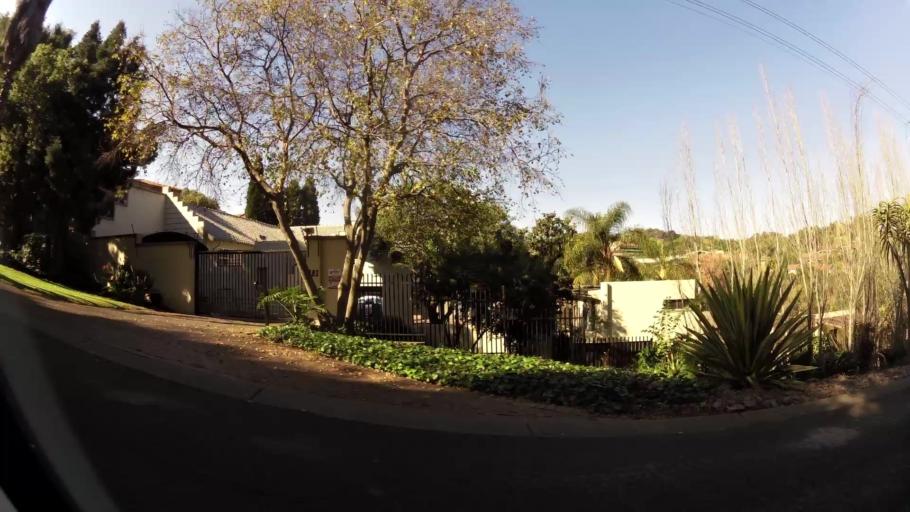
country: ZA
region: Gauteng
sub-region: City of Tshwane Metropolitan Municipality
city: Pretoria
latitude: -25.7905
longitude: 28.2508
